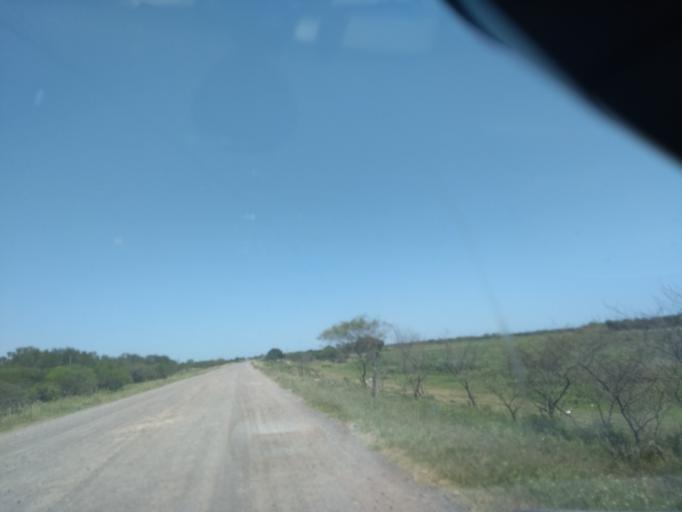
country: AR
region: Chaco
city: Resistencia
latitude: -27.4092
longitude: -58.9480
